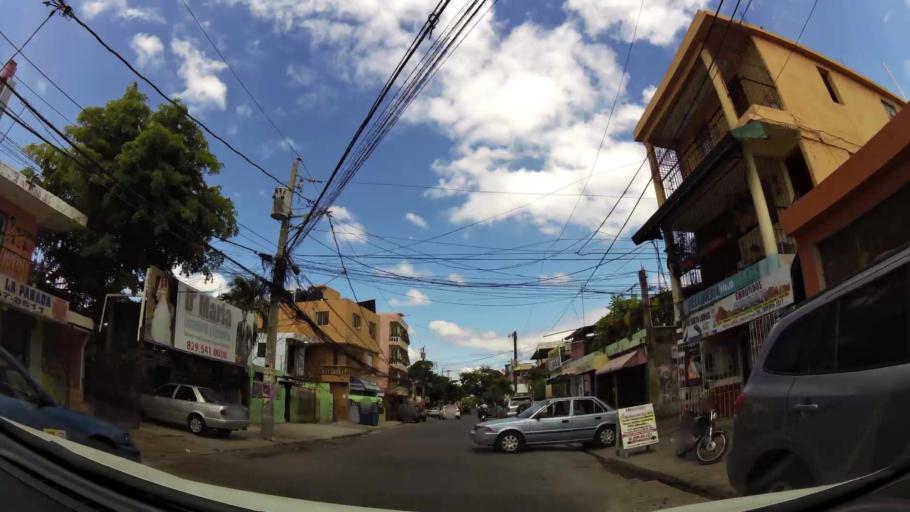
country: DO
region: Nacional
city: Bella Vista
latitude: 18.4661
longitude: -69.9473
